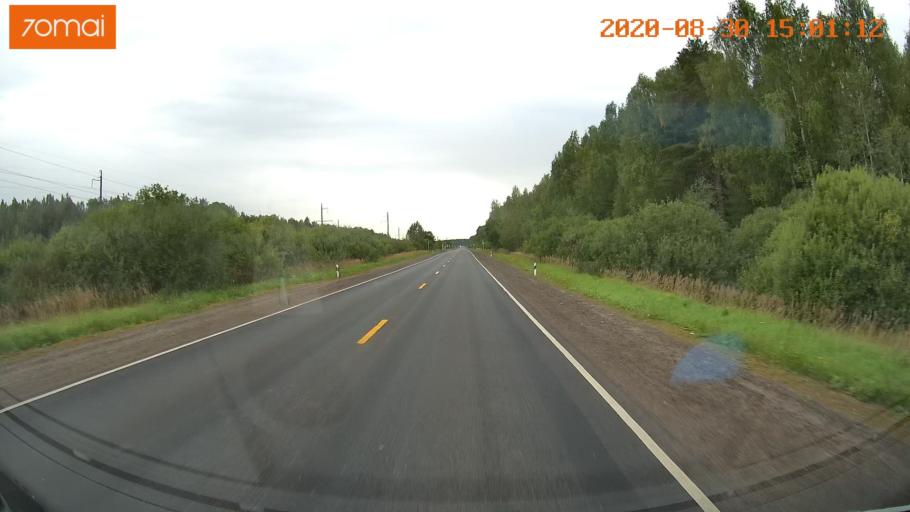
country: RU
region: Ivanovo
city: Staraya Vichuga
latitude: 57.3237
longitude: 41.9452
